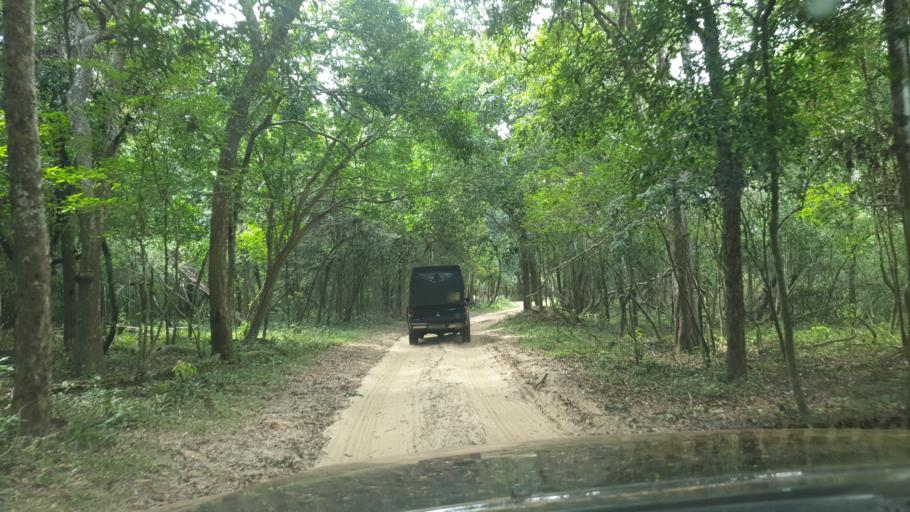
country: LK
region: North Western
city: Puttalam
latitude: 8.4129
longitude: 79.9910
